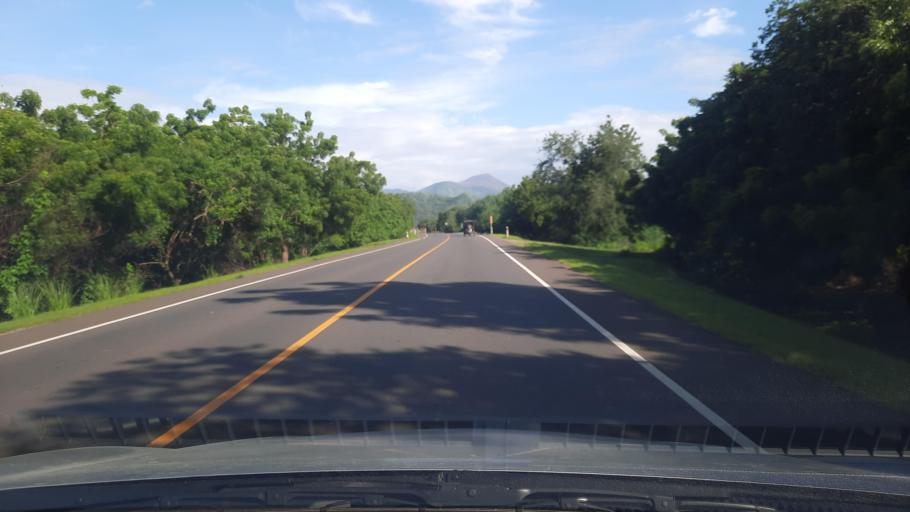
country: NI
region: Leon
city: Telica
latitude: 12.7176
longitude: -86.8760
